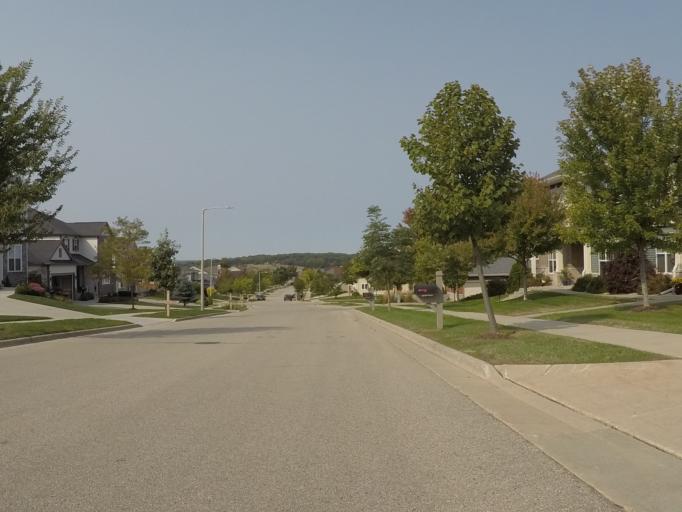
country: US
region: Wisconsin
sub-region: Dane County
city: Verona
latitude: 43.0301
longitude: -89.5475
